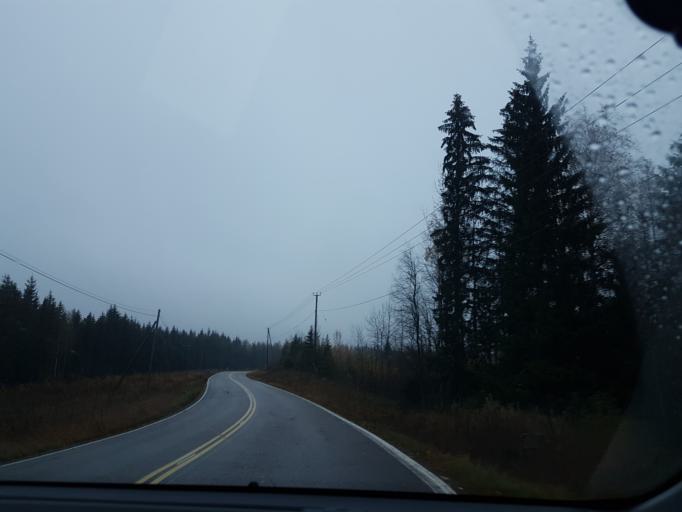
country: FI
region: Uusimaa
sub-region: Helsinki
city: Maentsaelae
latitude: 60.5953
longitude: 25.1988
